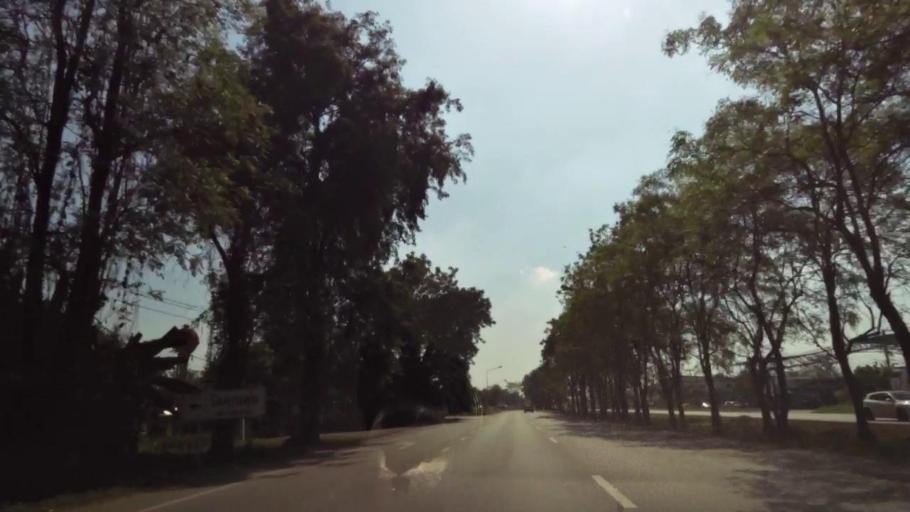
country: TH
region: Phichit
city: Bueng Na Rang
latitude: 16.1910
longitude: 100.1287
